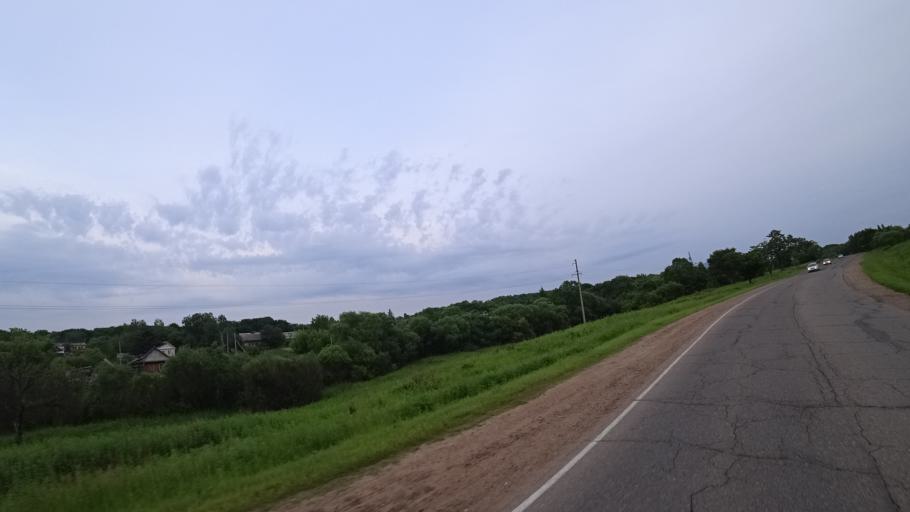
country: RU
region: Primorskiy
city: Novosysoyevka
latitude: 44.2248
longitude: 133.3509
